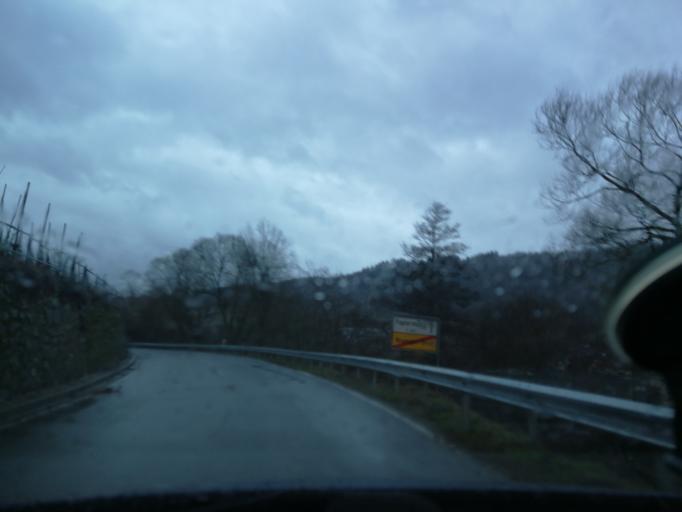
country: DE
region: Rheinland-Pfalz
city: Minheim
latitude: 49.8591
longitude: 6.9109
